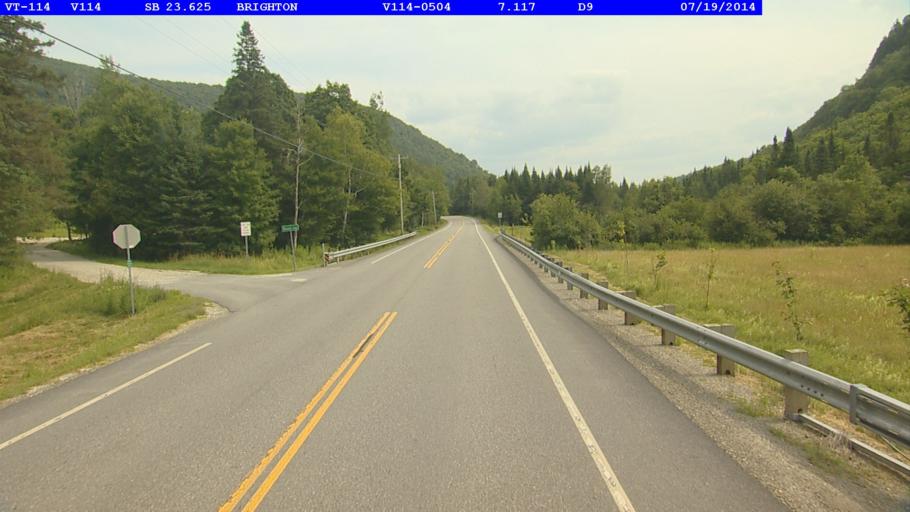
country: CA
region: Quebec
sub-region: Estrie
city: Coaticook
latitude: 44.8432
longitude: -71.9086
